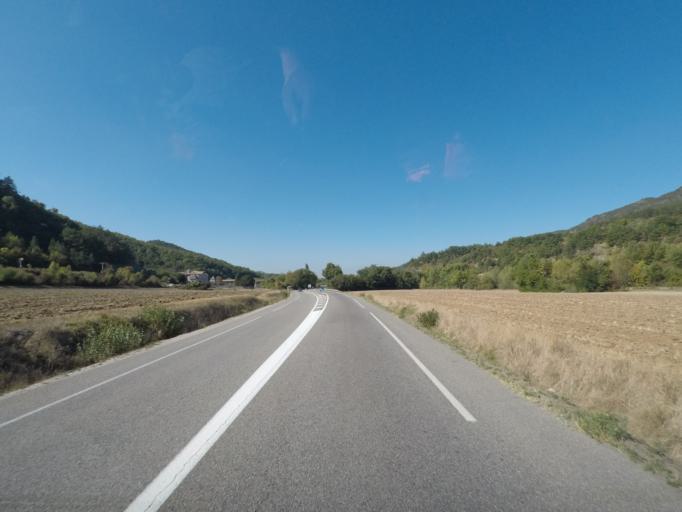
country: FR
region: Rhone-Alpes
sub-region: Departement de la Drome
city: Aouste-sur-Sye
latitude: 44.6926
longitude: 5.1780
